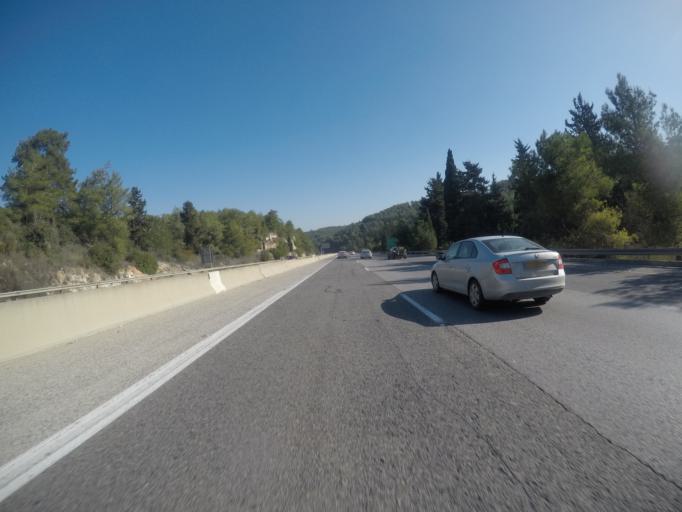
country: IL
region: Haifa
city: Daliyat el Karmil
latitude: 32.6406
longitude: 35.0708
